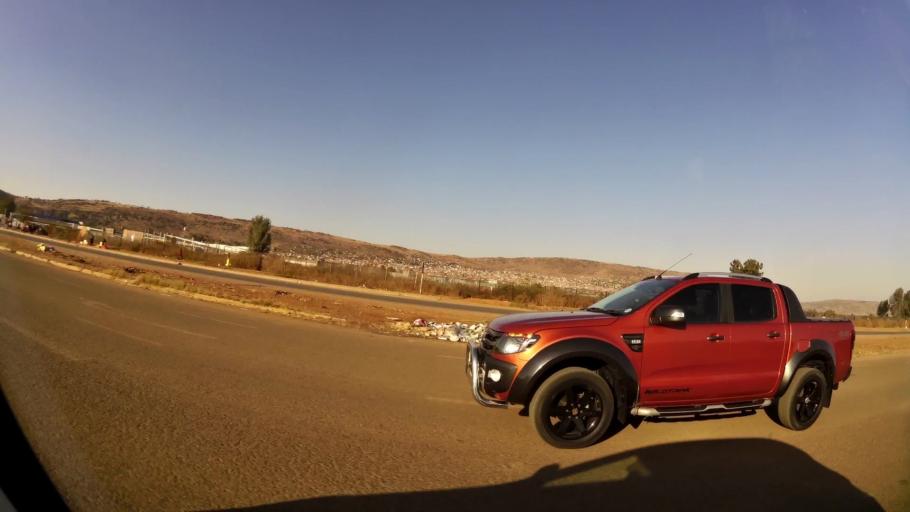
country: ZA
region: Gauteng
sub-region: City of Tshwane Metropolitan Municipality
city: Cullinan
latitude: -25.7043
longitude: 28.4185
